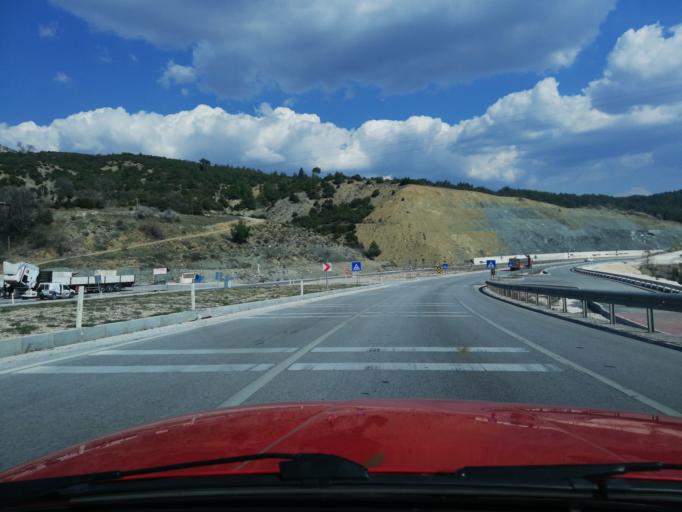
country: TR
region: Burdur
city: Celtikci
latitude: 37.5776
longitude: 30.4459
